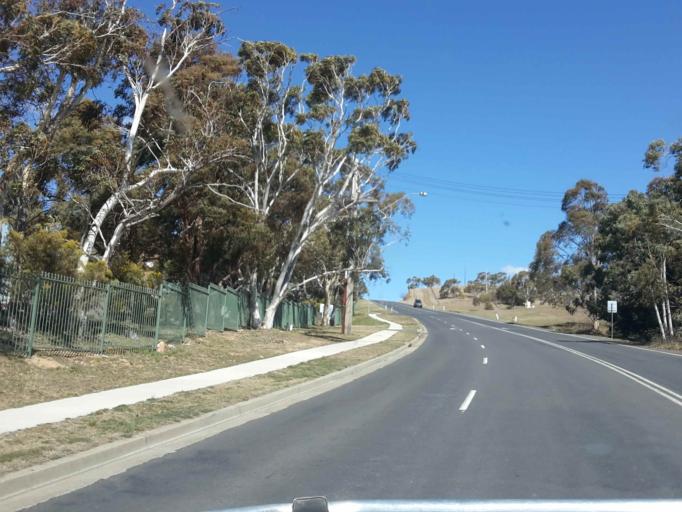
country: AU
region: New South Wales
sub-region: Snowy River
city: Jindabyne
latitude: -36.4180
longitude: 148.6107
